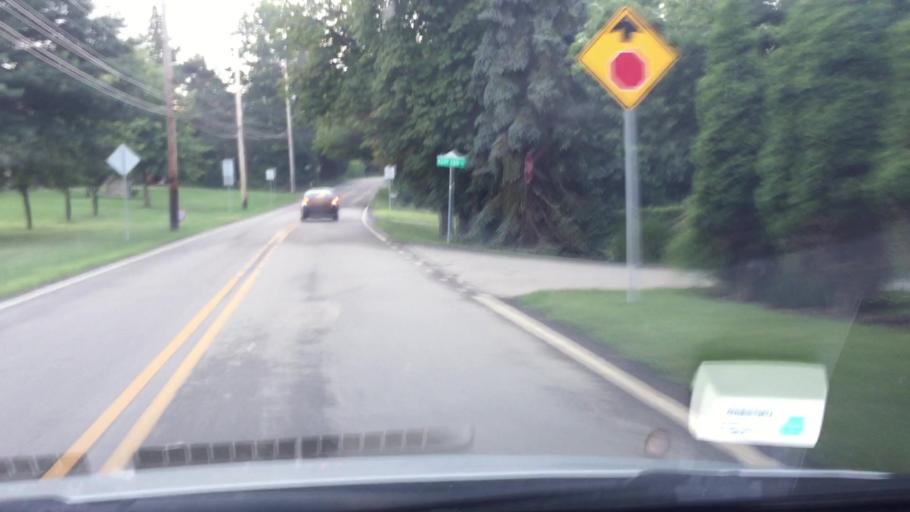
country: US
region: Pennsylvania
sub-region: Allegheny County
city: Allison Park
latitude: 40.5532
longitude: -79.9354
